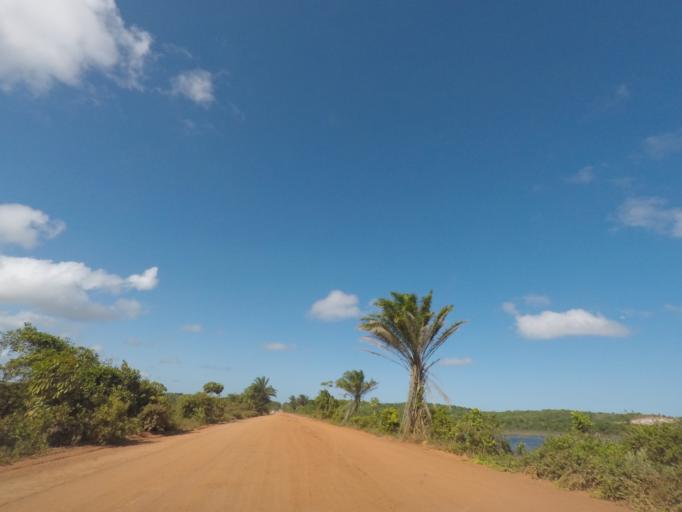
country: BR
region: Bahia
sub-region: Marau
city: Marau
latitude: -14.1442
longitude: -39.0025
